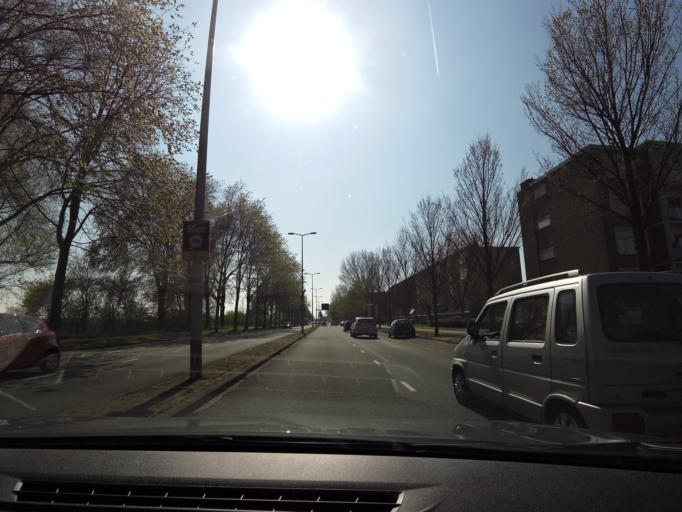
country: NL
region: South Holland
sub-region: Gemeente Westland
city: Kwintsheul
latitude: 52.0325
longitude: 4.2644
